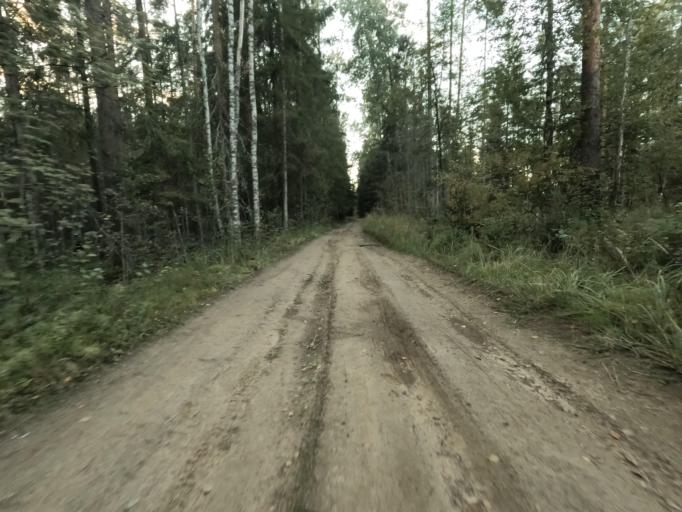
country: RU
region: Leningrad
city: Otradnoye
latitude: 59.8358
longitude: 30.8075
